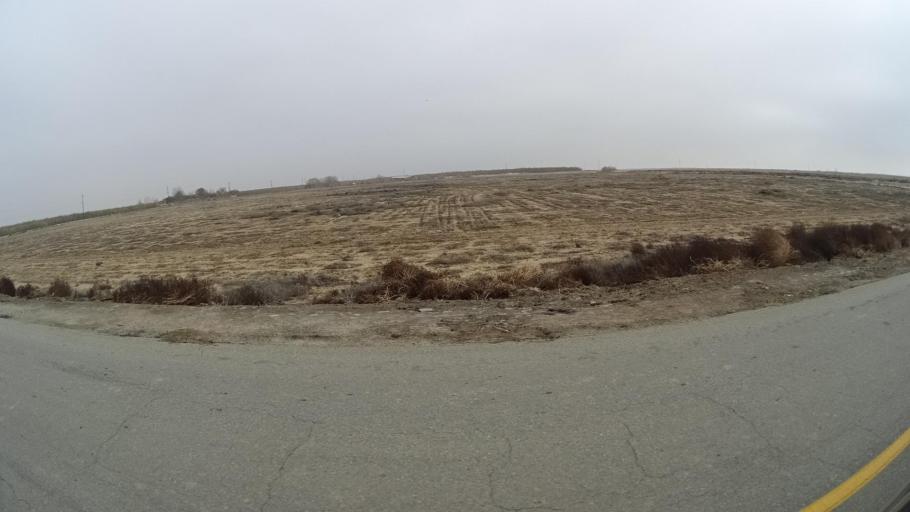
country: US
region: California
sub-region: Kern County
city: Maricopa
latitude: 35.0922
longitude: -119.3141
